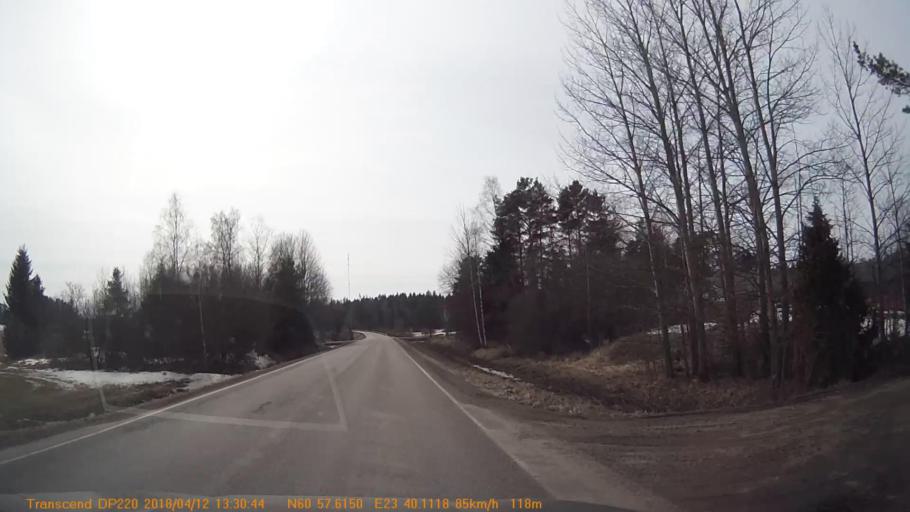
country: FI
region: Haeme
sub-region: Forssa
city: Forssa
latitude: 60.9601
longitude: 23.6683
